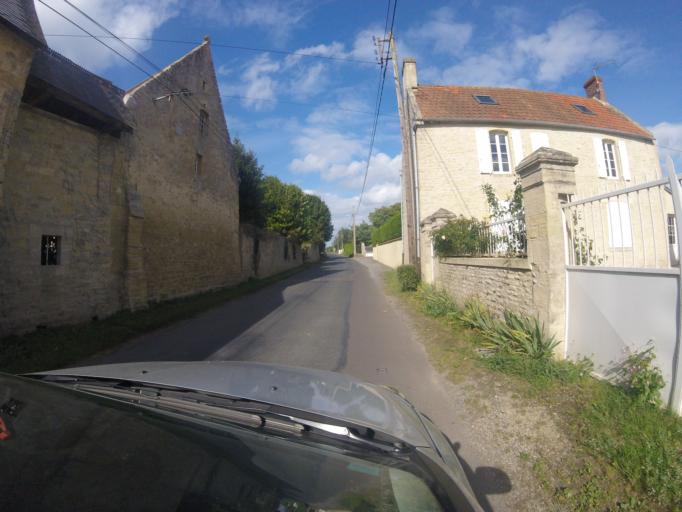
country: FR
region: Lower Normandy
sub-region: Departement du Calvados
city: Saint-Vigor-le-Grand
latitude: 49.3402
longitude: -0.6917
